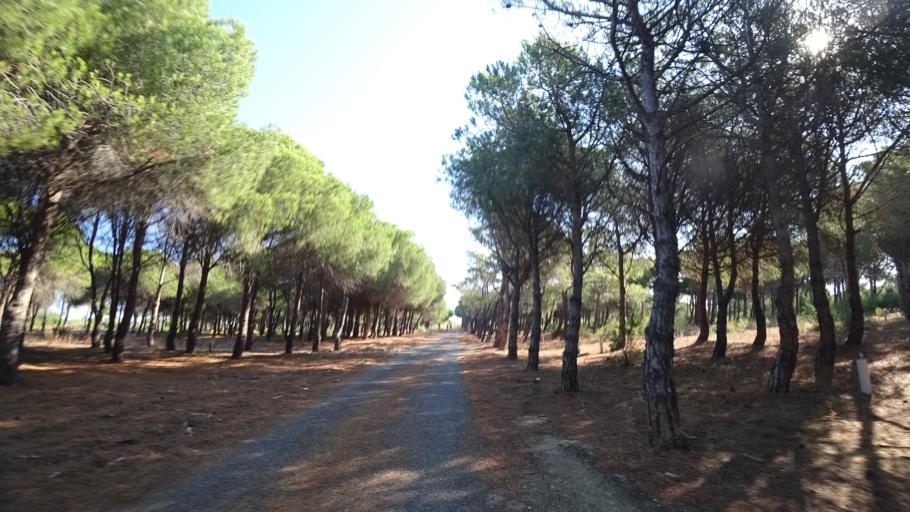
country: FR
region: Languedoc-Roussillon
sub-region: Departement de l'Aude
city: Leucate
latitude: 42.8710
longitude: 3.0365
